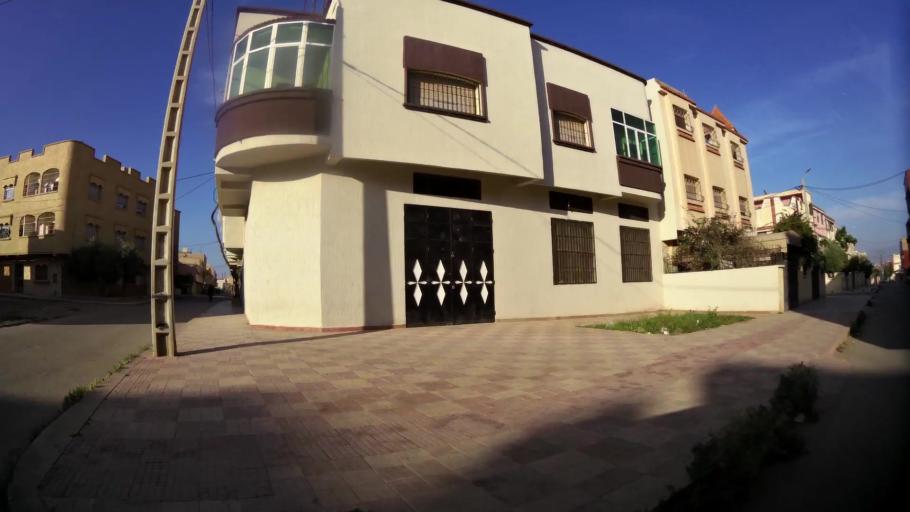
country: MA
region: Oriental
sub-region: Oujda-Angad
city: Oujda
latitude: 34.7068
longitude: -1.8962
